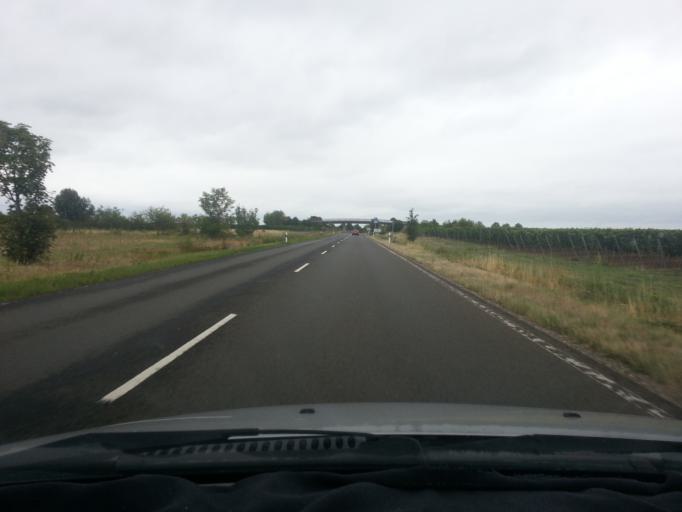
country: DE
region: Rheinland-Pfalz
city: Wachenheim
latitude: 49.4507
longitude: 8.1923
